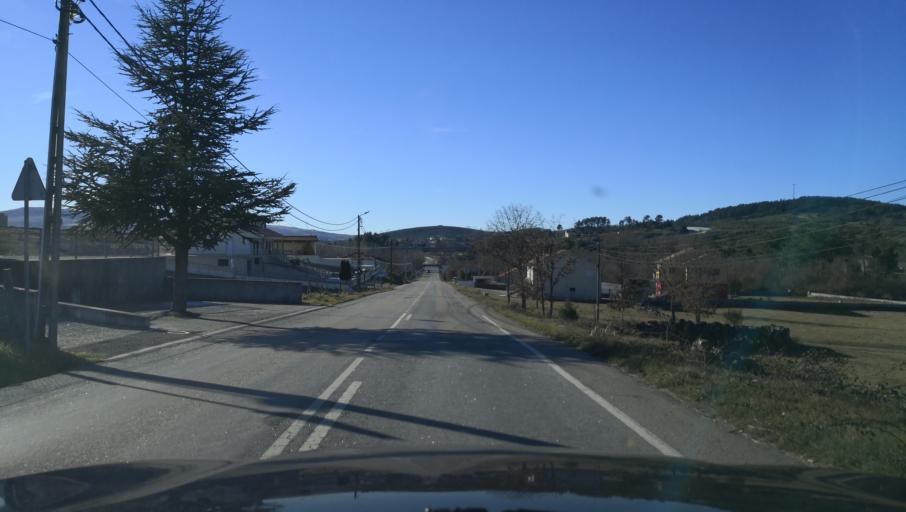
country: PT
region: Vila Real
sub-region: Vila Pouca de Aguiar
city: Vila Pouca de Aguiar
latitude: 41.5012
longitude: -7.6963
